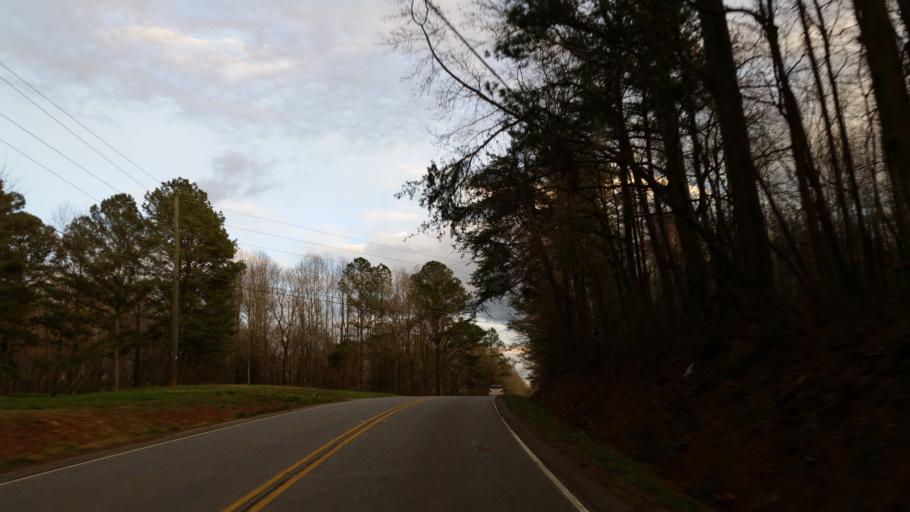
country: US
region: Georgia
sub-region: Pickens County
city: Jasper
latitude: 34.4674
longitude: -84.4841
